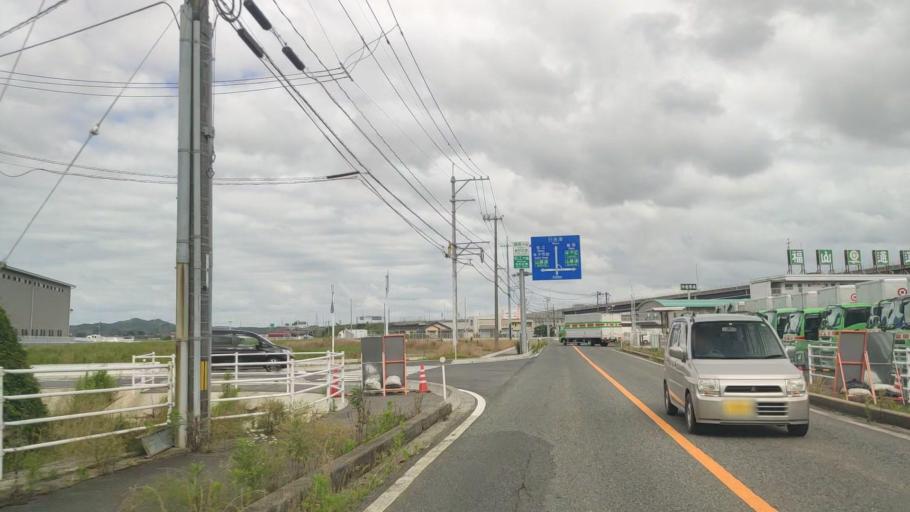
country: JP
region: Tottori
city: Yonago
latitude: 35.4239
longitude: 133.3995
